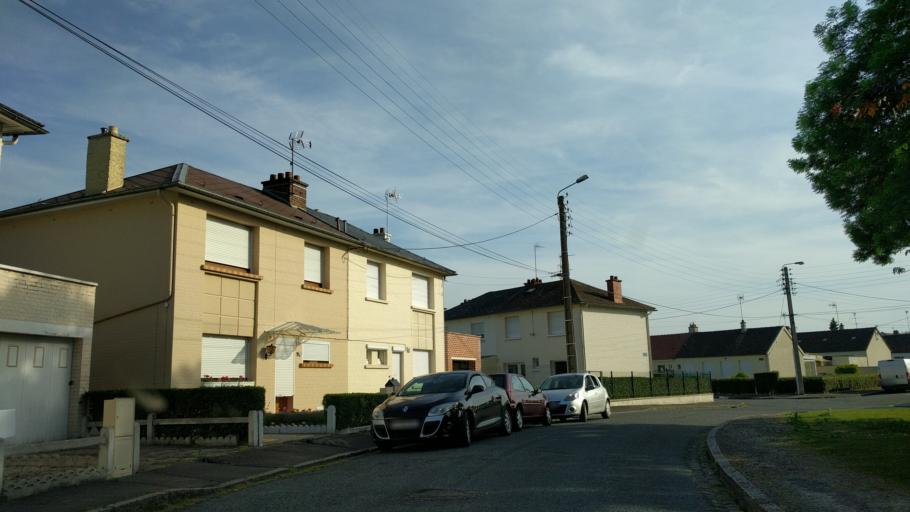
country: FR
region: Picardie
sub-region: Departement de la Somme
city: Peronne
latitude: 49.9348
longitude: 2.9458
